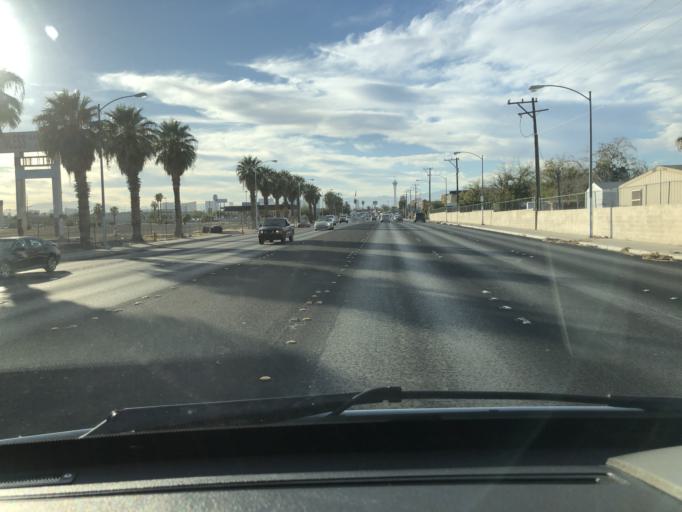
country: US
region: Nevada
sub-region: Clark County
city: Winchester
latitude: 36.1463
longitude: -115.0972
